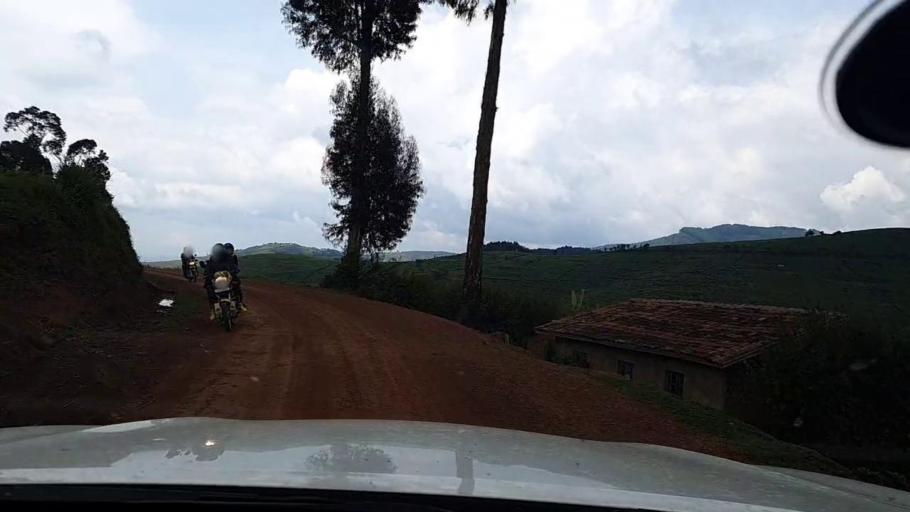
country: RW
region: Western Province
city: Kibuye
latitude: -2.1726
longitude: 29.4394
